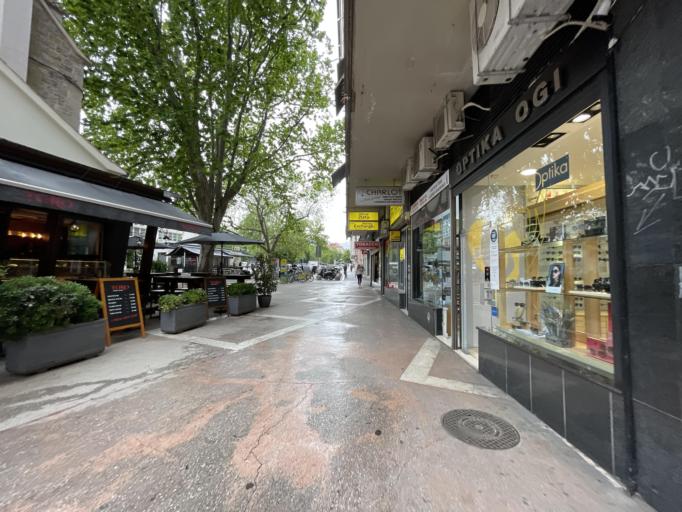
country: HR
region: Splitsko-Dalmatinska
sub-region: Grad Split
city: Split
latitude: 43.5116
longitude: 16.4364
